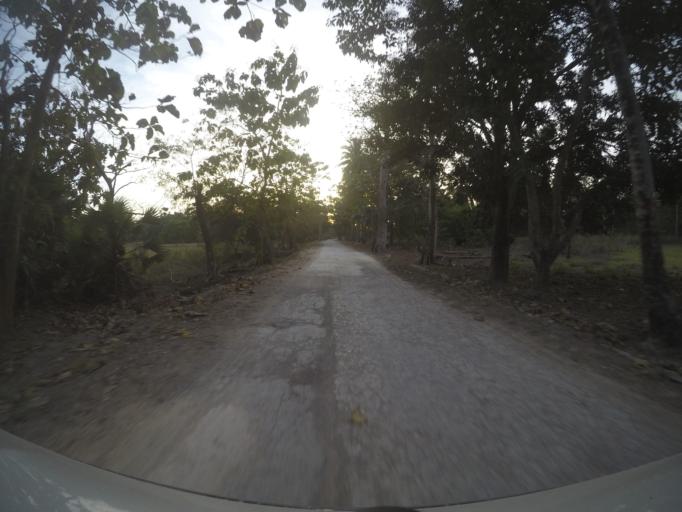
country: TL
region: Viqueque
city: Viqueque
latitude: -8.9430
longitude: 126.4327
